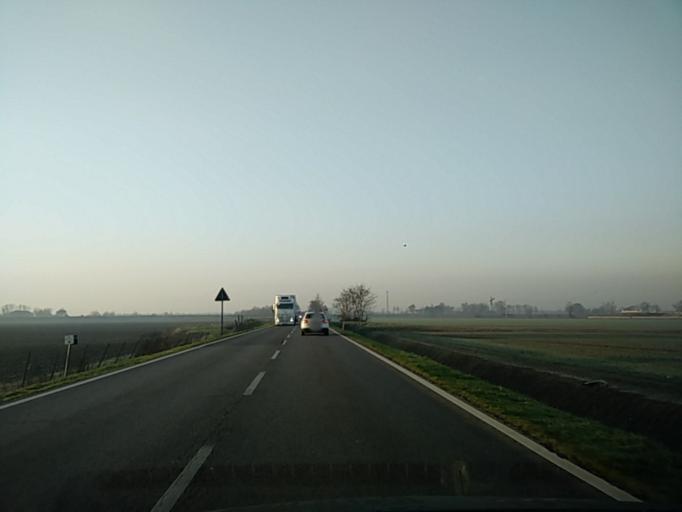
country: IT
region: Veneto
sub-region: Provincia di Venezia
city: Quarto d'Altino
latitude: 45.5418
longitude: 12.4034
